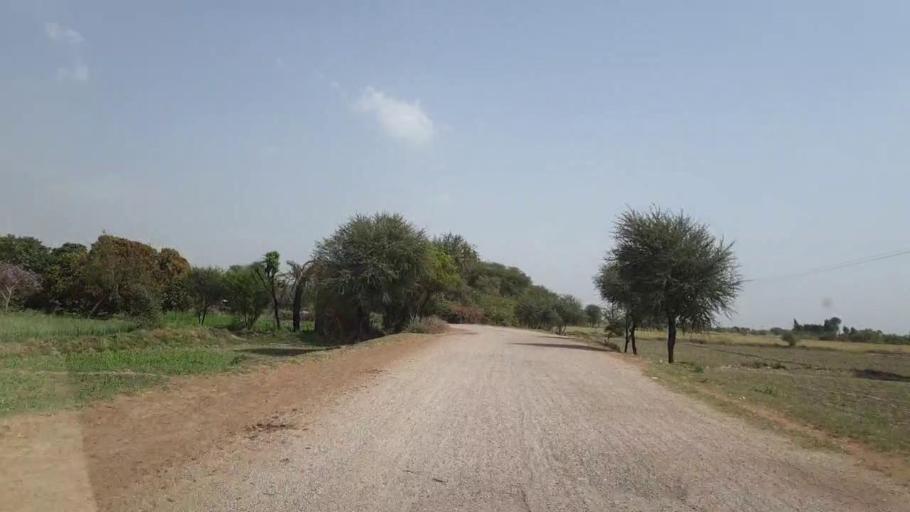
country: PK
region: Sindh
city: Rajo Khanani
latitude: 25.0506
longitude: 68.8626
